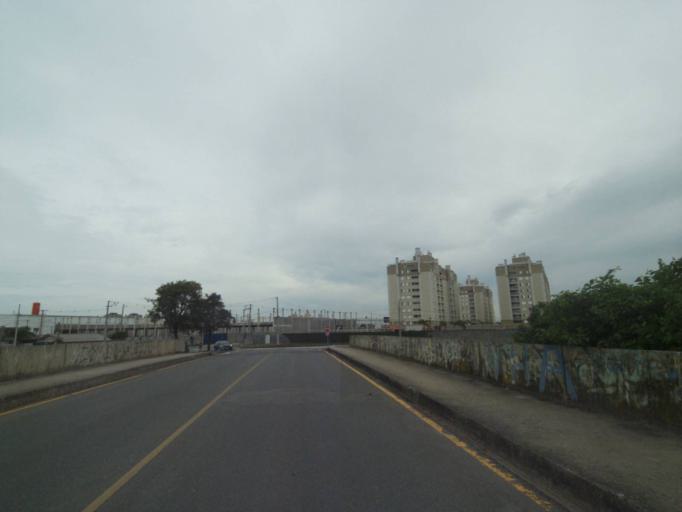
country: BR
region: Parana
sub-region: Pinhais
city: Pinhais
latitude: -25.4286
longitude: -49.2013
